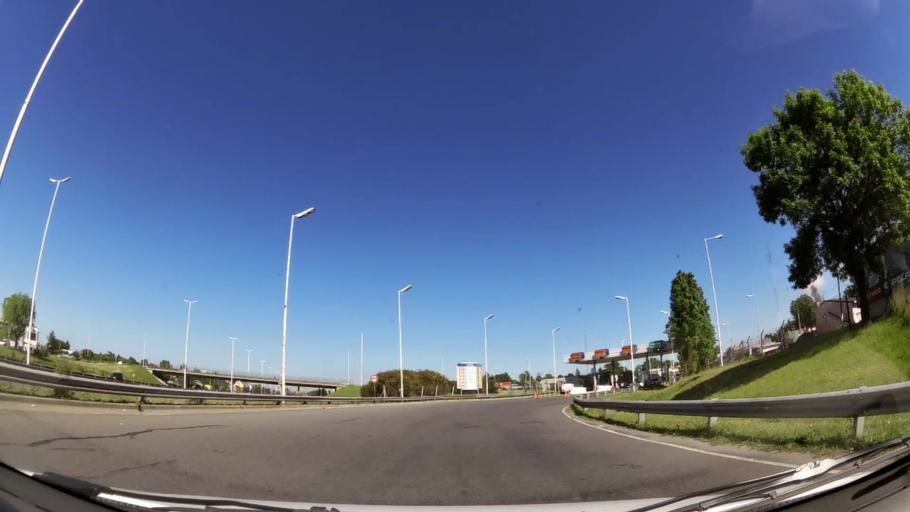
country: AR
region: Buenos Aires
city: Ituzaingo
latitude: -34.6310
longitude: -58.6519
